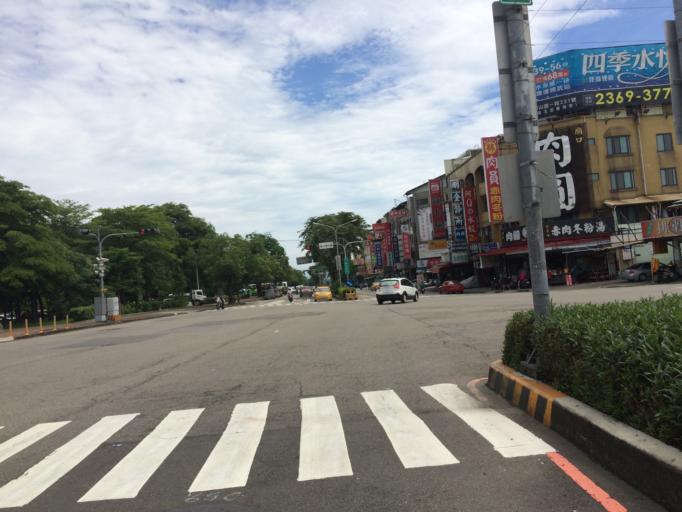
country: TW
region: Taiwan
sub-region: Taichung City
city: Taichung
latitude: 24.1405
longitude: 120.6966
